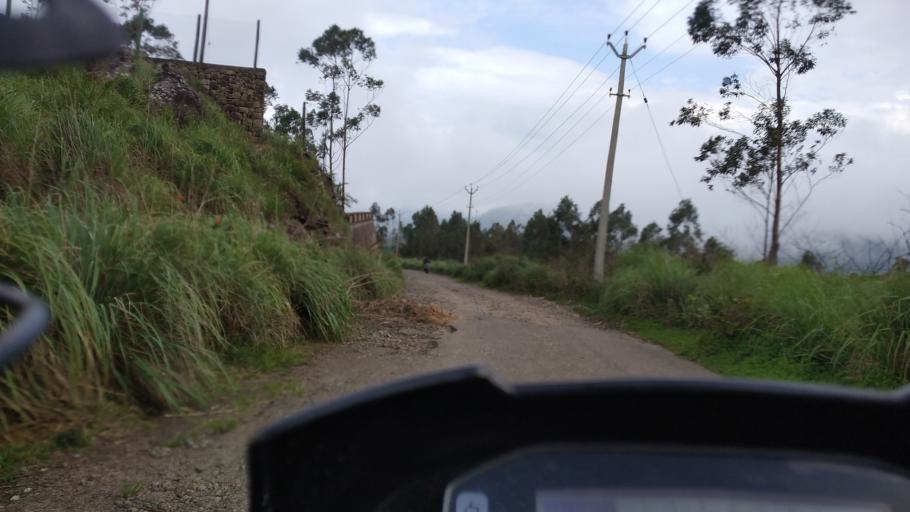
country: IN
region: Kerala
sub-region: Idukki
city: Munnar
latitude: 10.0398
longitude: 77.1804
